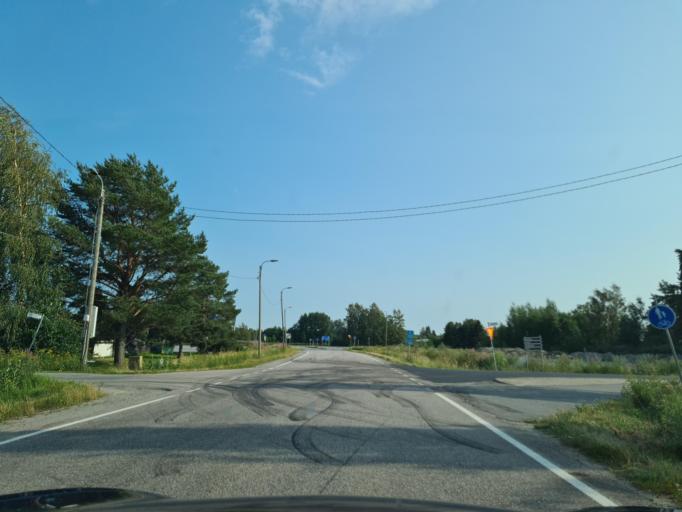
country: FI
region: Ostrobothnia
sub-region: Vaasa
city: Vaehaekyroe
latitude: 63.0075
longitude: 22.1494
